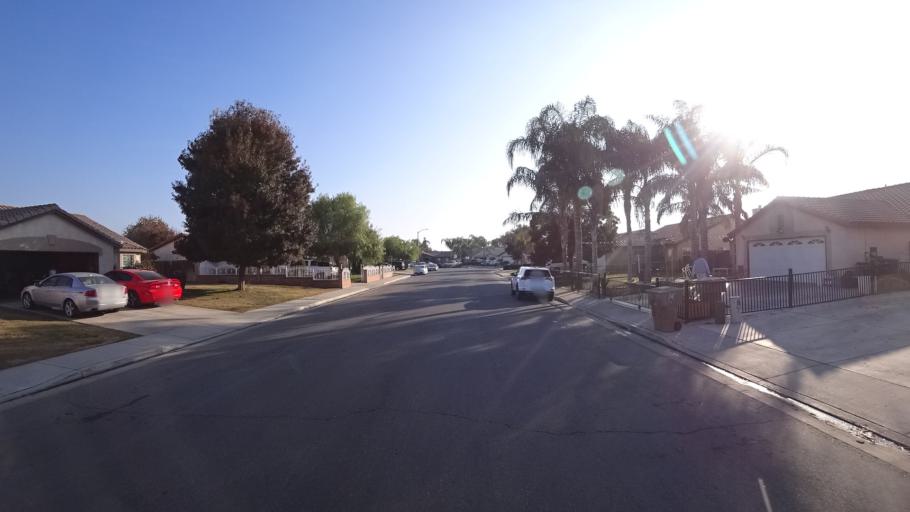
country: US
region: California
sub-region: Kern County
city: Greenfield
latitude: 35.2862
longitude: -119.0093
